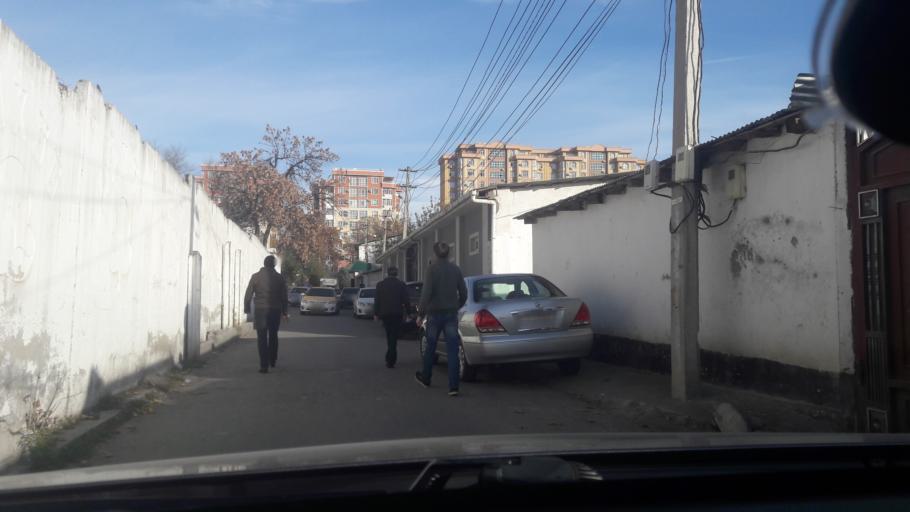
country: TJ
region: Dushanbe
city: Dushanbe
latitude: 38.5826
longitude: 68.7596
